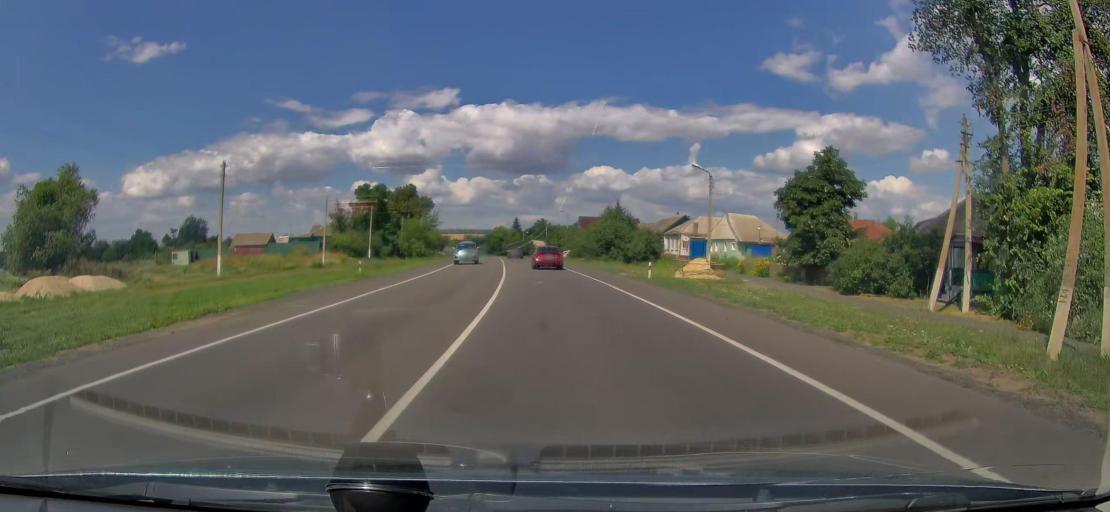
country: RU
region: Kursk
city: Zolotukhino
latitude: 51.9343
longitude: 36.3091
